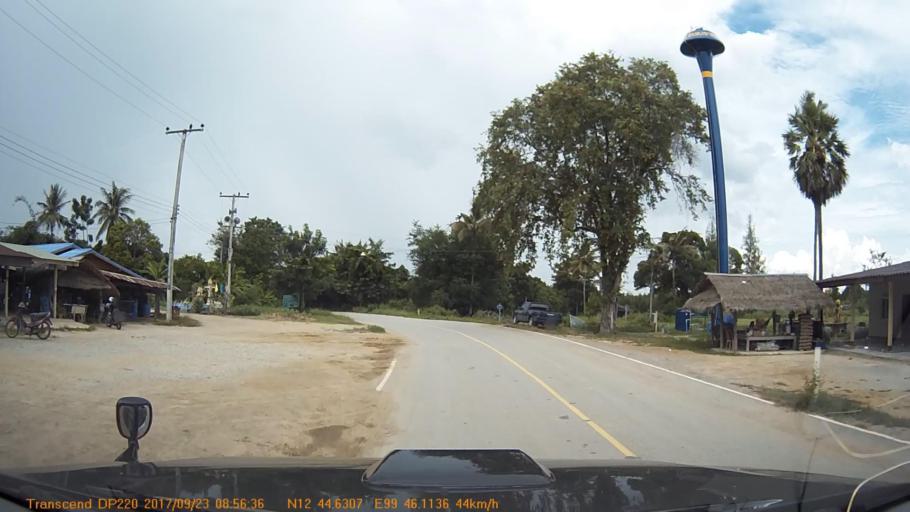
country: TH
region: Phetchaburi
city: Kaeng Krachan
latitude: 12.7438
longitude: 99.7686
